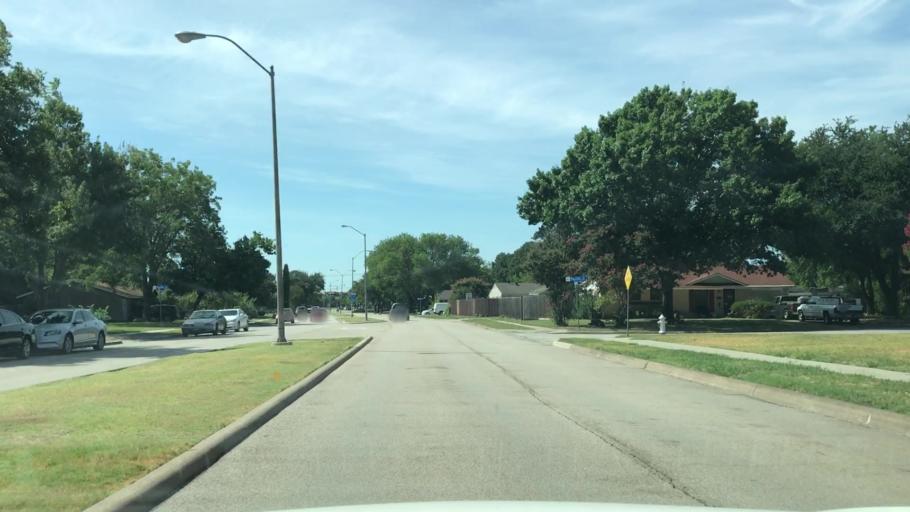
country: US
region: Texas
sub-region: Dallas County
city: Richardson
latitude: 32.9507
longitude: -96.7142
